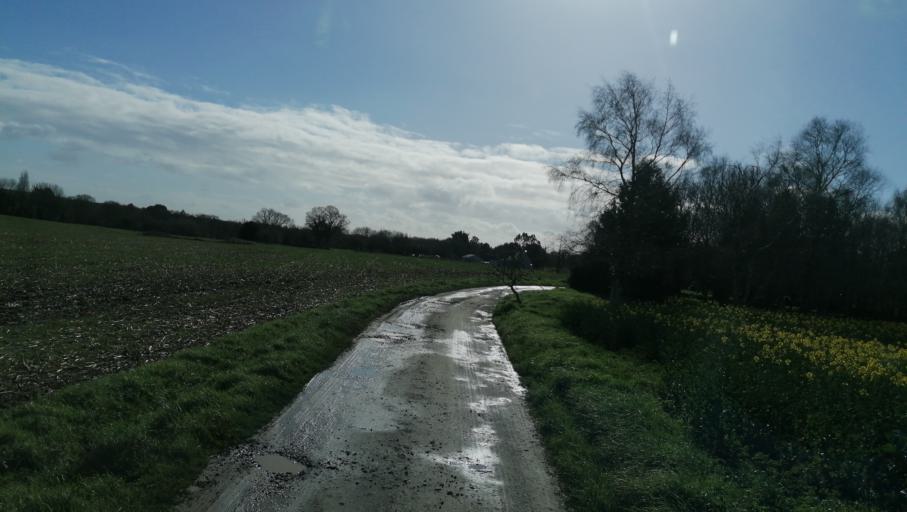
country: FR
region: Brittany
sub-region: Departement des Cotes-d'Armor
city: Plouha
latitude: 48.6595
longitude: -2.9234
